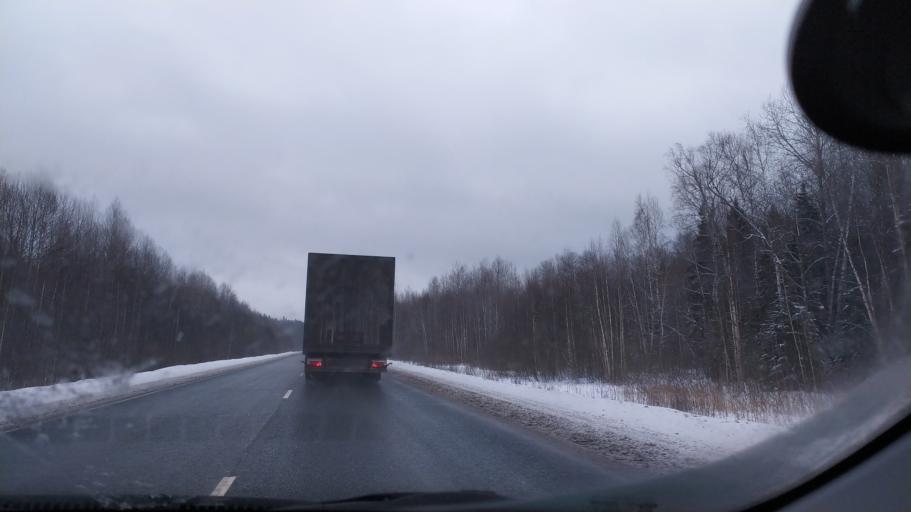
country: RU
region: Chuvashia
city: Mariinskiy Posad
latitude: 56.1877
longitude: 47.8228
